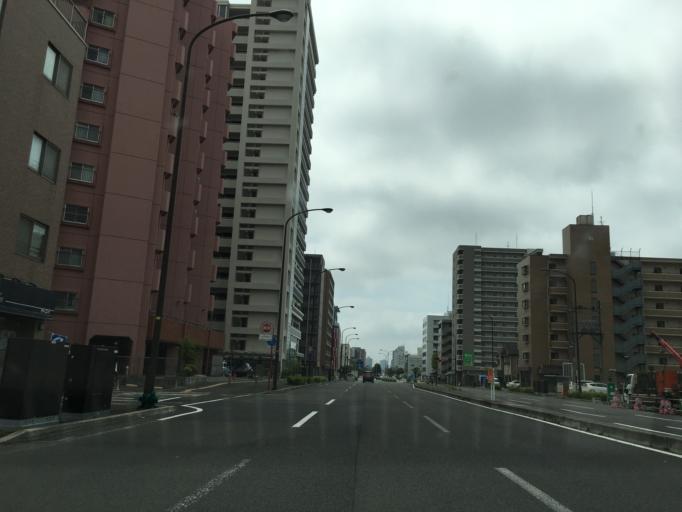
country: JP
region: Miyagi
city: Sendai-shi
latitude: 38.2620
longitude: 140.8923
